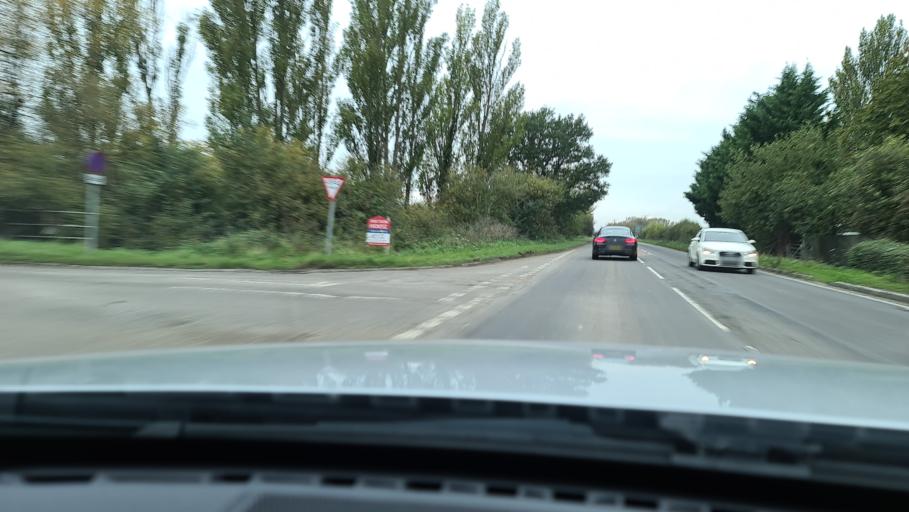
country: GB
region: England
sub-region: Buckinghamshire
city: Steeple Claydon
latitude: 51.8730
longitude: -1.0520
